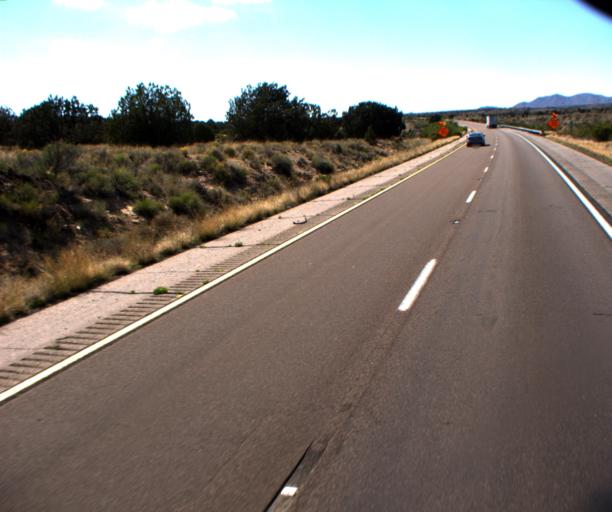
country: US
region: Arizona
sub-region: Mohave County
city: New Kingman-Butler
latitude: 35.1406
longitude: -113.6749
